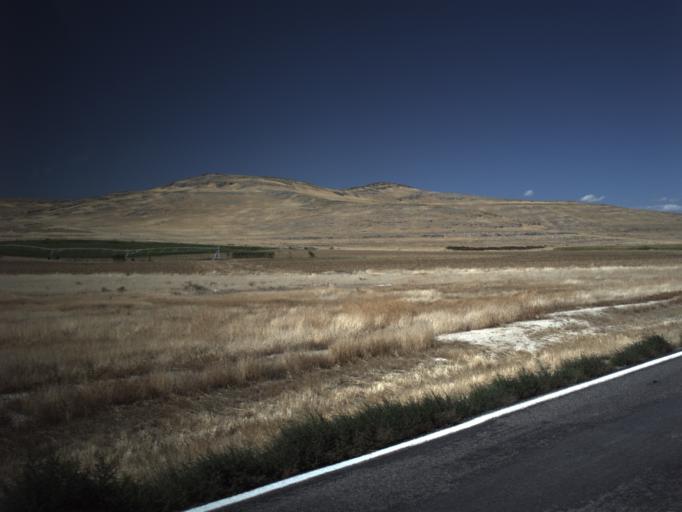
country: US
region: Utah
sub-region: Utah County
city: Genola
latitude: 40.1195
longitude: -111.9591
